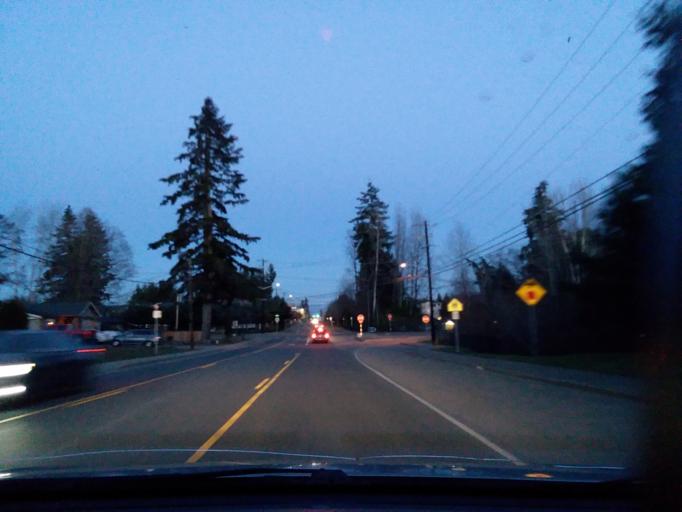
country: US
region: Washington
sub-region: Snohomish County
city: Martha Lake
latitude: 47.9073
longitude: -122.2482
